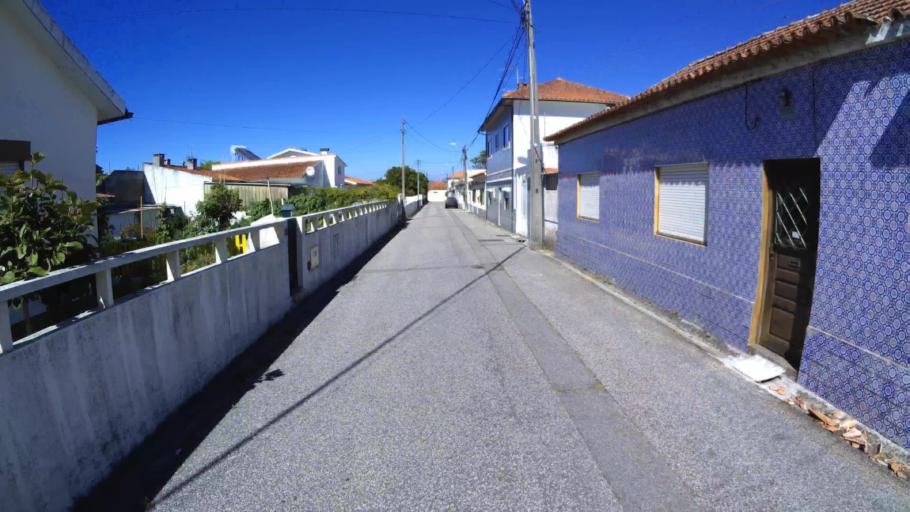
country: PT
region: Aveiro
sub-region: Aveiro
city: Aveiro
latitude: 40.6551
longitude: -8.6261
